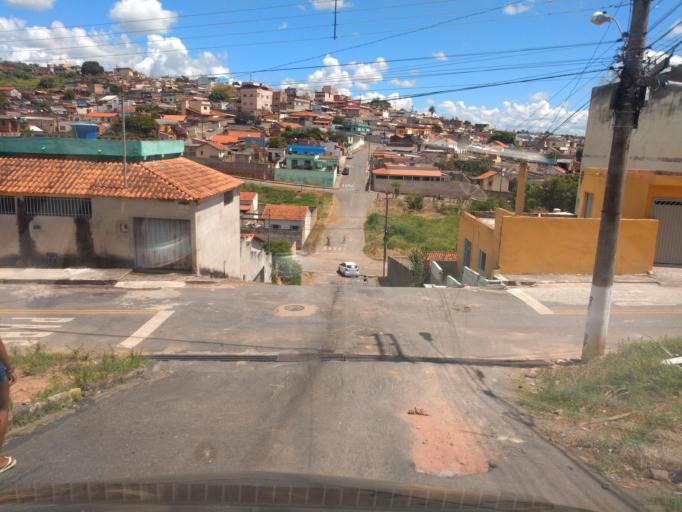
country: BR
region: Minas Gerais
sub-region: Tres Coracoes
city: Tres Coracoes
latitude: -21.6838
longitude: -45.2503
